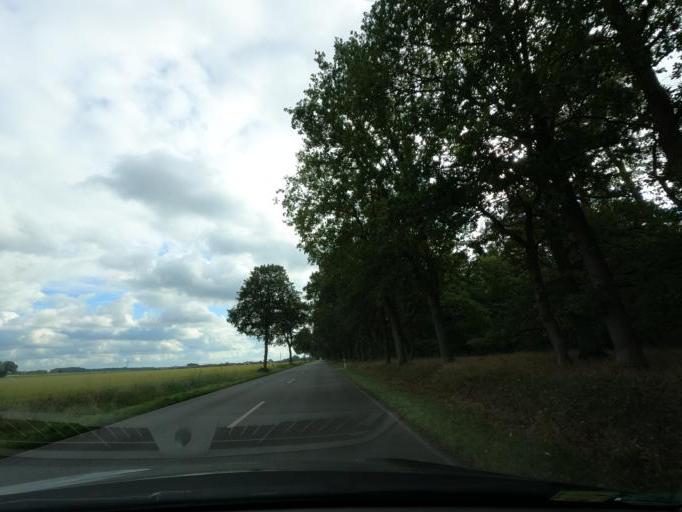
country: DE
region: Lower Saxony
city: Klein Schwulper
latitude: 52.3672
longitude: 10.4262
